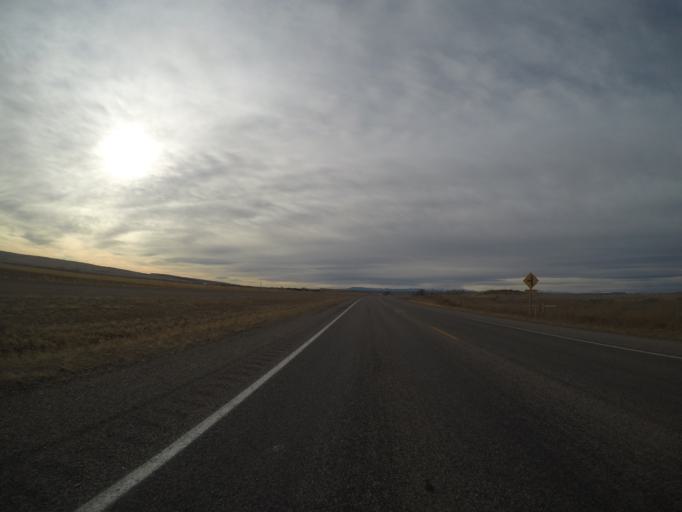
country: US
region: Montana
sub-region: Yellowstone County
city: Laurel
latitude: 45.6269
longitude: -108.8035
